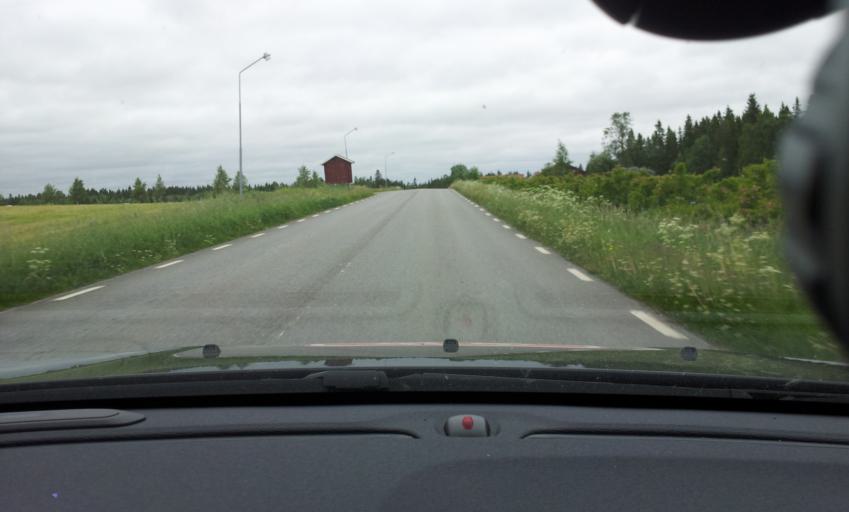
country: SE
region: Jaemtland
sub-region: Bergs Kommun
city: Hoverberg
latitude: 63.0377
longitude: 14.3443
